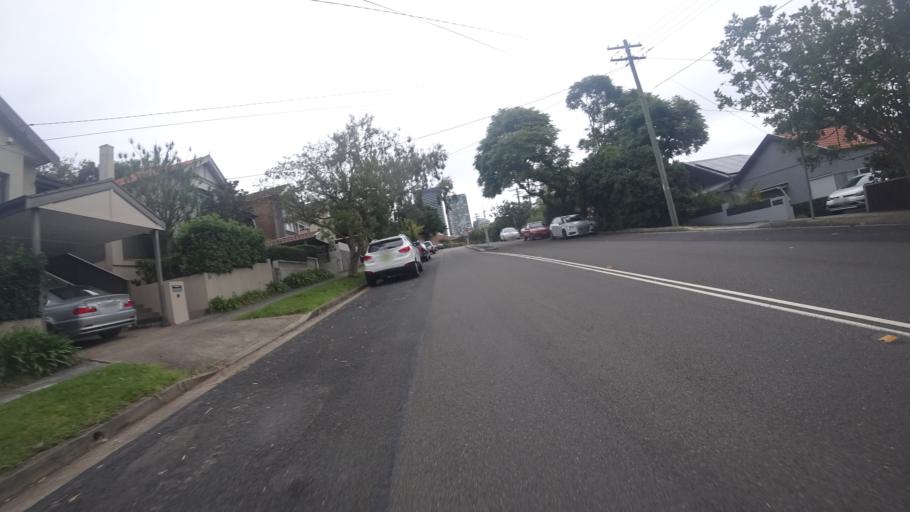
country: AU
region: New South Wales
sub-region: North Sydney
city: St Leonards
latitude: -33.8177
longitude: 151.1980
